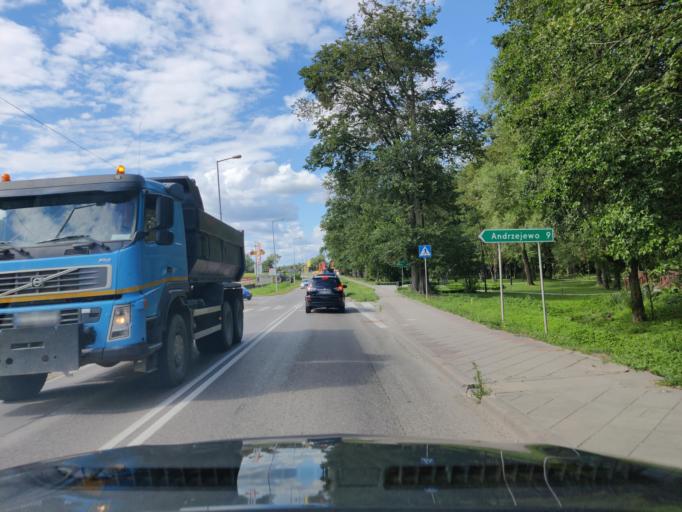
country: PL
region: Podlasie
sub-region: Powiat wysokomazowiecki
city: Czyzew
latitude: 52.8004
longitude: 22.3110
